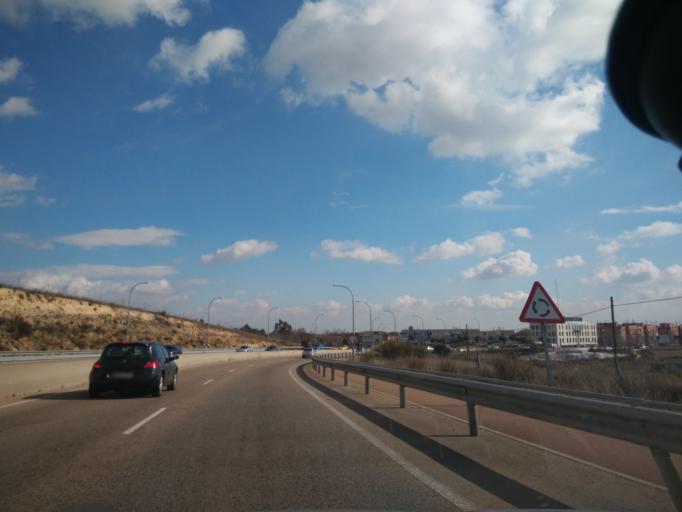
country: ES
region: Madrid
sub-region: Provincia de Madrid
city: Alcobendas
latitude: 40.5502
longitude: -3.6651
